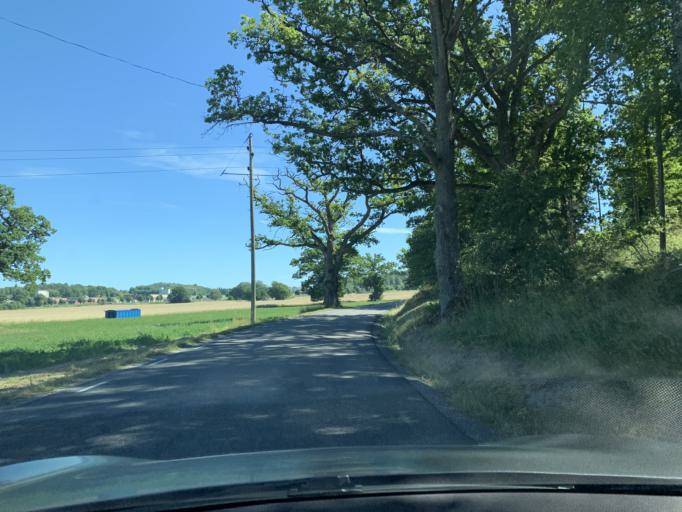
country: SE
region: Stockholm
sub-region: Botkyrka Kommun
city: Eriksberg
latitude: 59.2506
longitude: 17.7781
